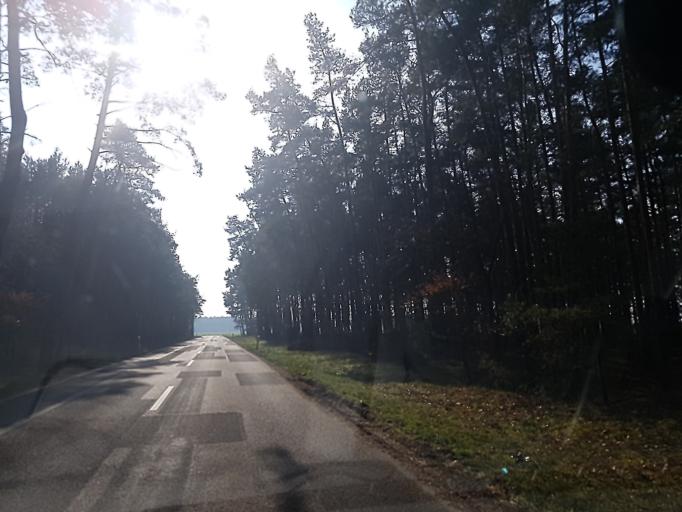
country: DE
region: Brandenburg
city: Wenzlow
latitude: 52.3106
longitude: 12.4405
